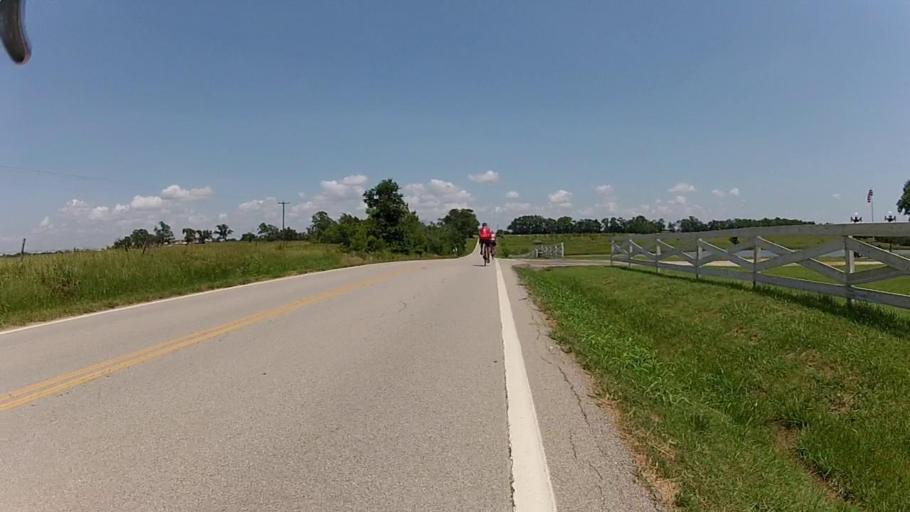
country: US
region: Kansas
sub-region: Montgomery County
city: Cherryvale
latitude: 37.1929
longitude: -95.4810
